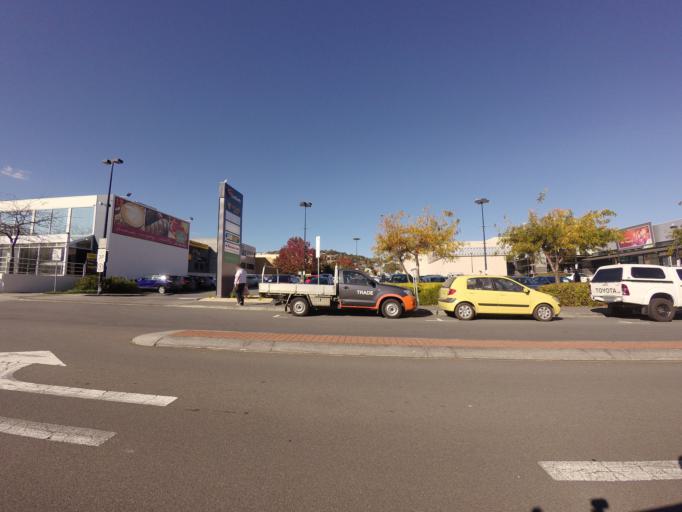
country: AU
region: Tasmania
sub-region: Clarence
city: Bellerive
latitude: -42.8668
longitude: 147.3689
